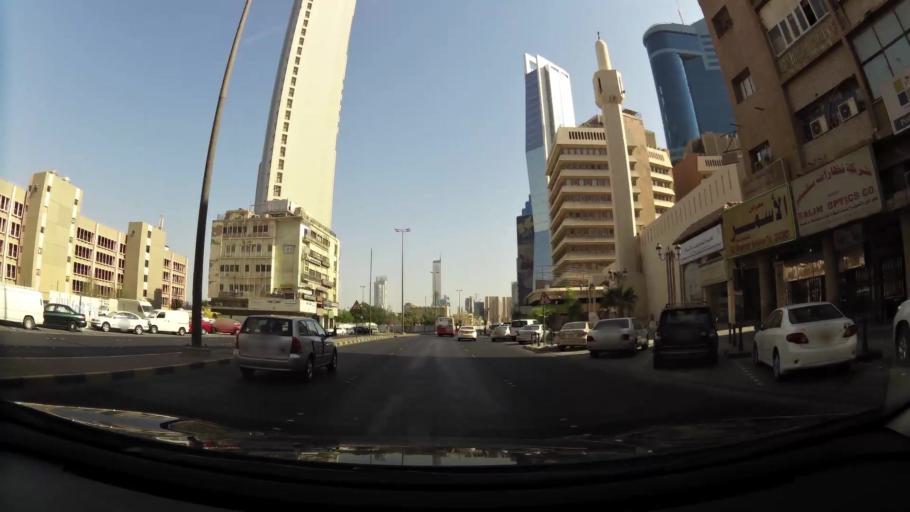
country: KW
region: Al Asimah
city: Kuwait City
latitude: 29.3679
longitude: 47.9683
